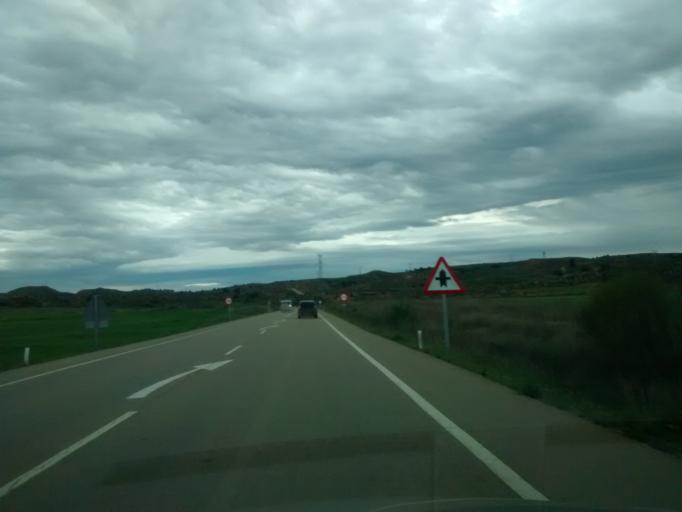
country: ES
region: Aragon
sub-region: Provincia de Zaragoza
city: Caspe
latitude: 41.1890
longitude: 0.0472
